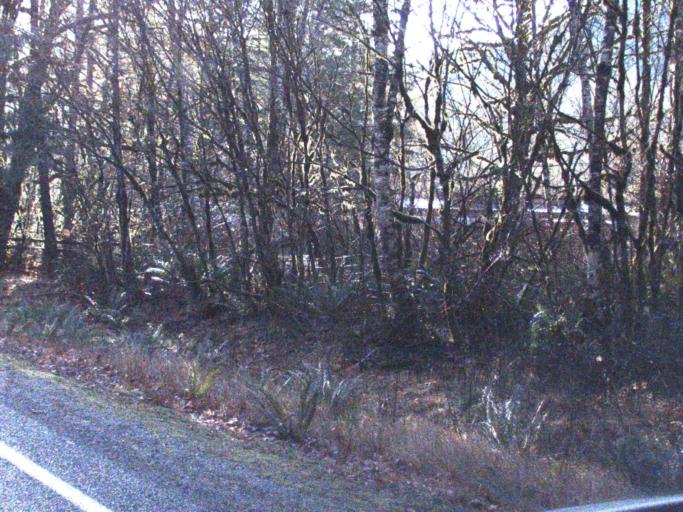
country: US
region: Washington
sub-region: Snohomish County
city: Darrington
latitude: 48.4382
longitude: -121.5768
